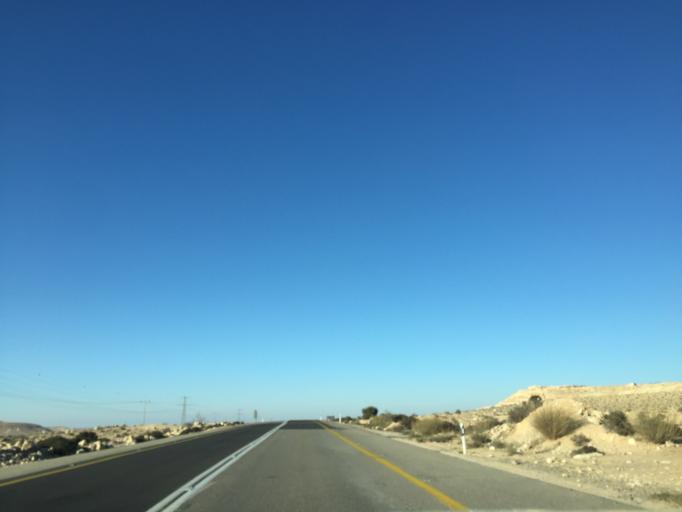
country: IL
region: Southern District
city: Midreshet Ben-Gurion
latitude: 30.7807
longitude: 34.7691
